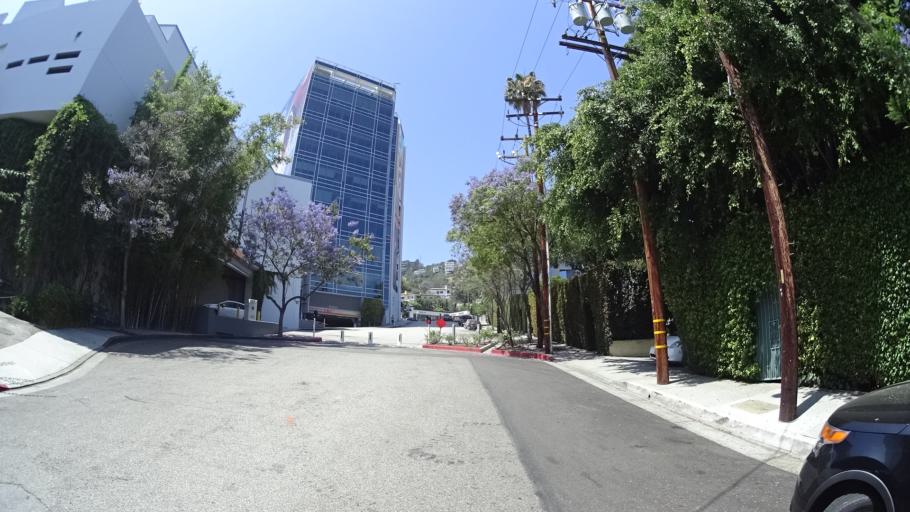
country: US
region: California
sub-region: Los Angeles County
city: West Hollywood
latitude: 34.0924
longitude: -118.3778
